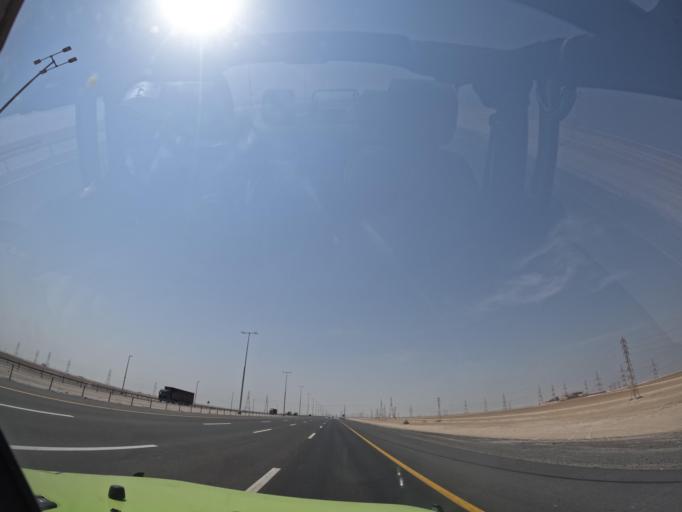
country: AE
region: Abu Dhabi
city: Abu Dhabi
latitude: 24.1563
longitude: 54.3124
